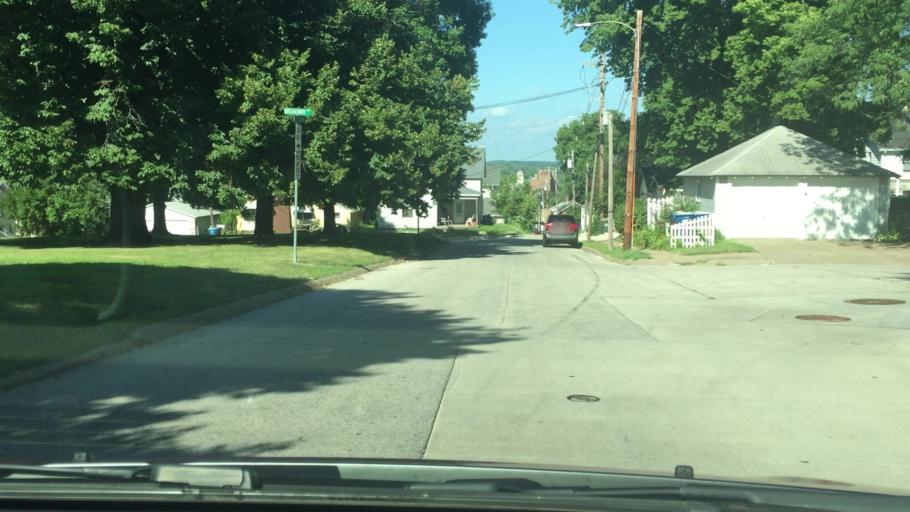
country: US
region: Iowa
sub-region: Muscatine County
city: Muscatine
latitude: 41.4188
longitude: -91.0535
